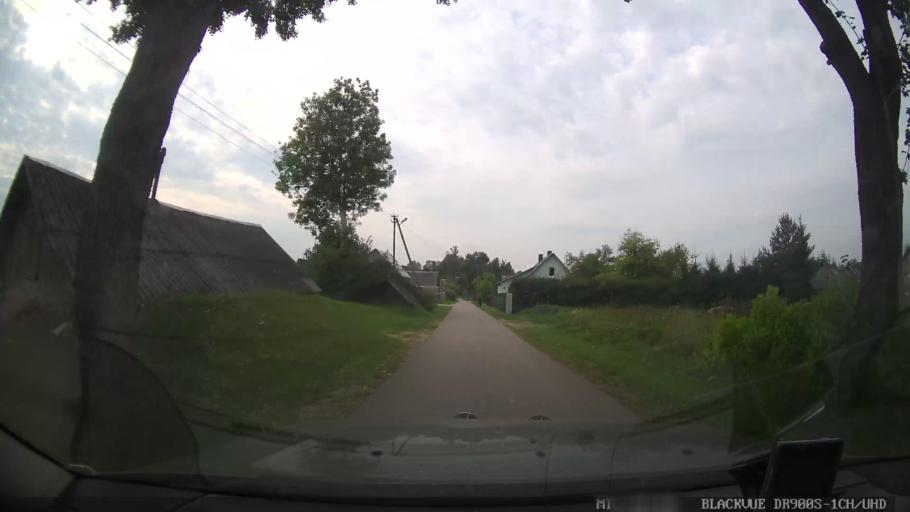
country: BY
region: Grodnenskaya
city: Ashmyany
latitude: 54.5314
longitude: 25.6682
